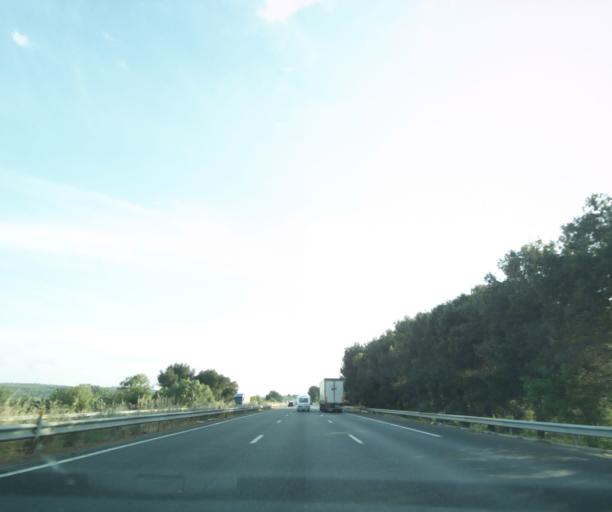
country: FR
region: Languedoc-Roussillon
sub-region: Departement de l'Aude
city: Fleury
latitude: 43.2477
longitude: 3.1533
